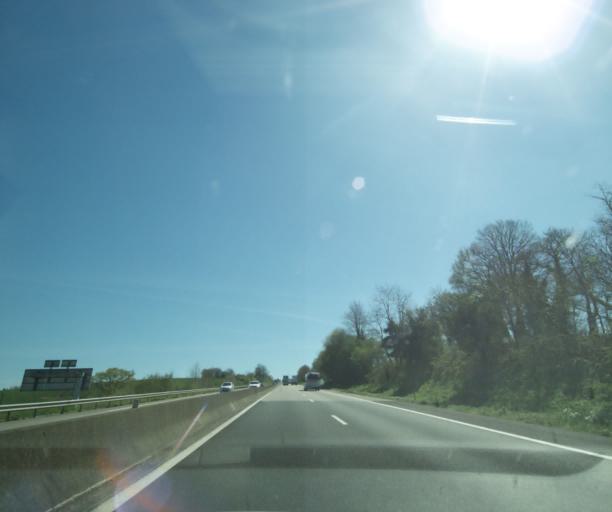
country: FR
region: Limousin
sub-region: Departement de la Haute-Vienne
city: Pierre-Buffiere
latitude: 45.7209
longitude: 1.3508
